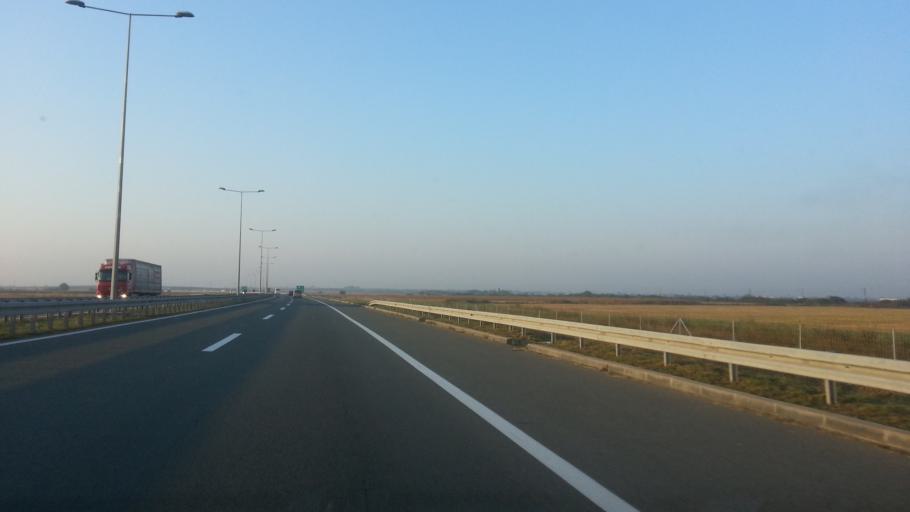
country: RS
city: Dobanovci
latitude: 44.8596
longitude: 20.2503
